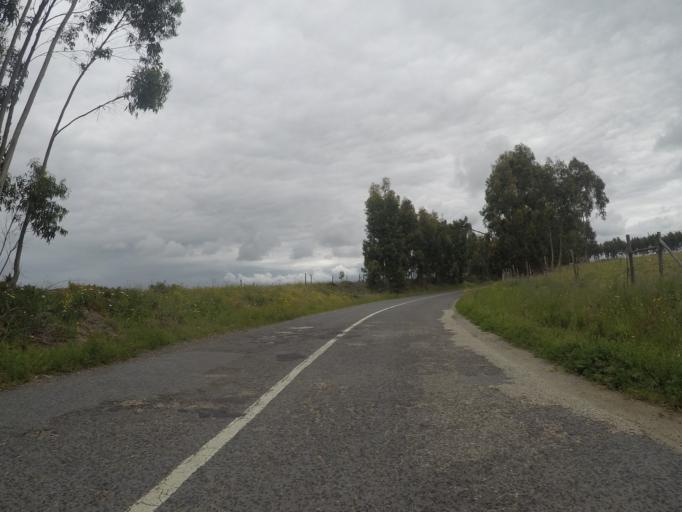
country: PT
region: Beja
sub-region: Odemira
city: Sao Teotonio
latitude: 37.5939
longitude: -8.7773
